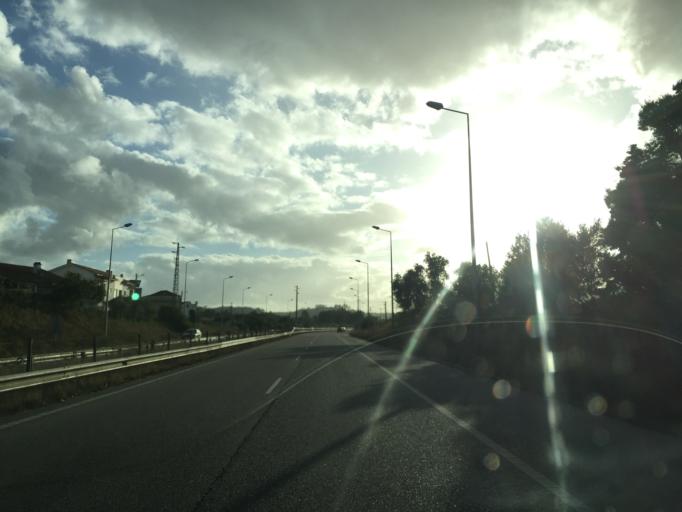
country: PT
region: Coimbra
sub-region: Coimbra
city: Coimbra
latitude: 40.2116
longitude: -8.4632
